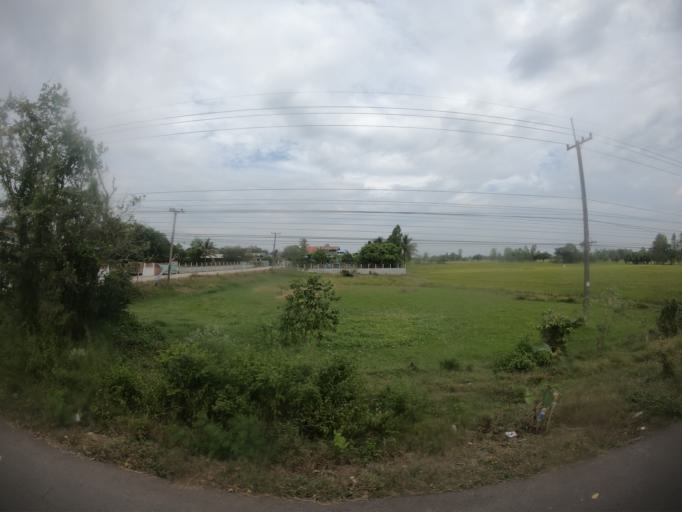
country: TH
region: Kalasin
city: Khong Chai
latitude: 16.1382
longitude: 103.4384
